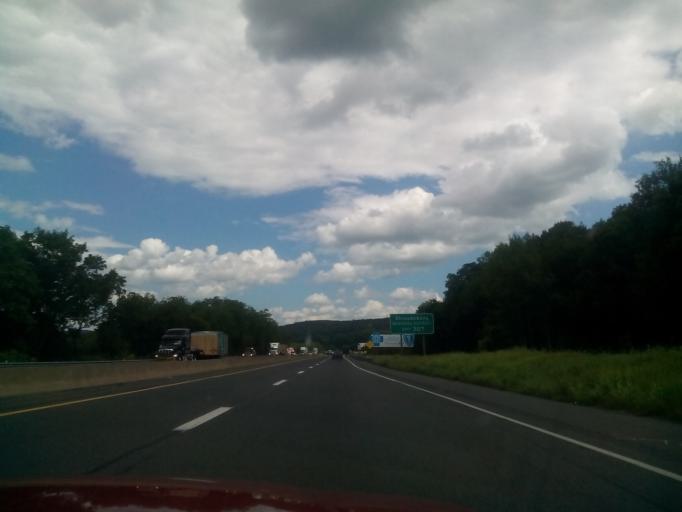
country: US
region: Pennsylvania
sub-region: Monroe County
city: Arlington Heights
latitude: 40.9810
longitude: -75.2099
